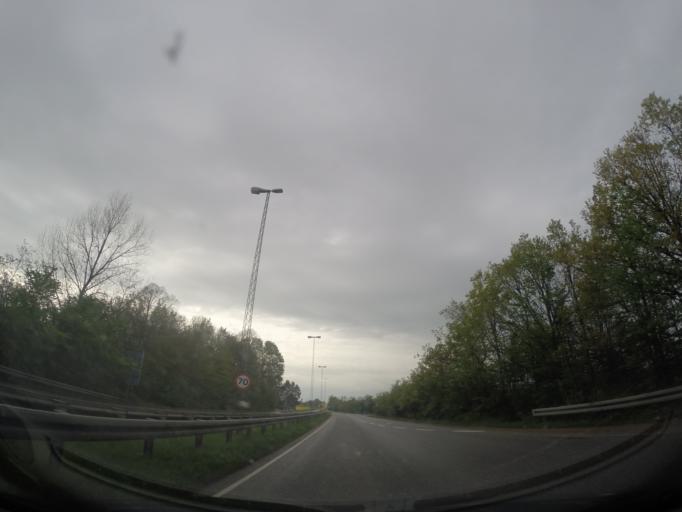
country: DK
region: Capital Region
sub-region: Hoje-Taastrup Kommune
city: Taastrup
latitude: 55.6654
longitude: 12.2799
